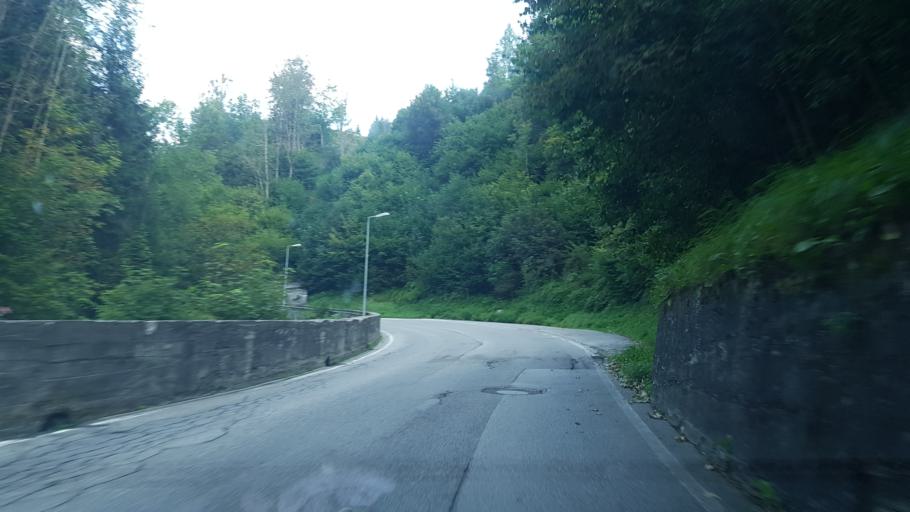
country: IT
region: Veneto
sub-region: Provincia di Belluno
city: San Pietro di Cadore
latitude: 46.5696
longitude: 12.5851
